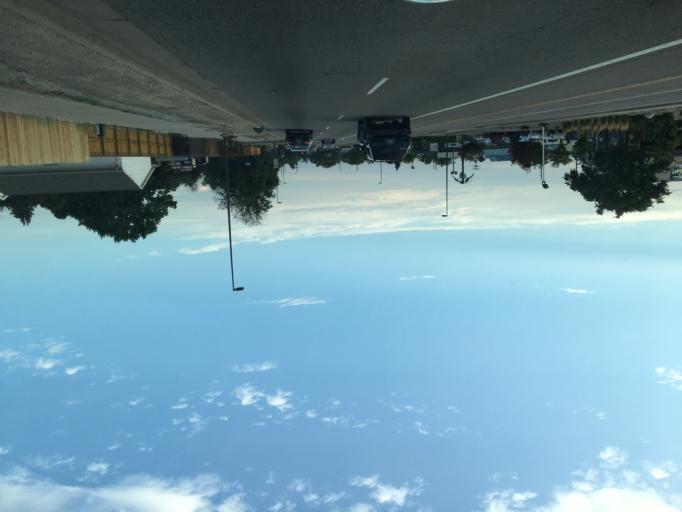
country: US
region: Colorado
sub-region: Adams County
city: Aurora
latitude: 39.7229
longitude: -104.8659
